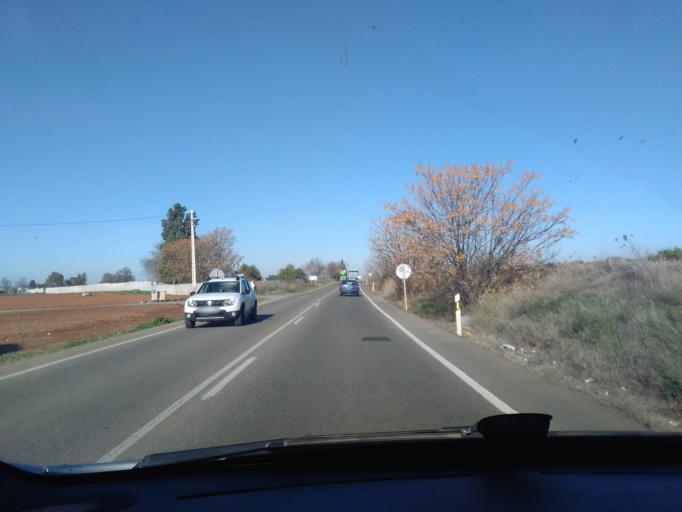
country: ES
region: Andalusia
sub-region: Provincia de Sevilla
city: La Rinconada
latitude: 37.4394
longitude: -5.9391
